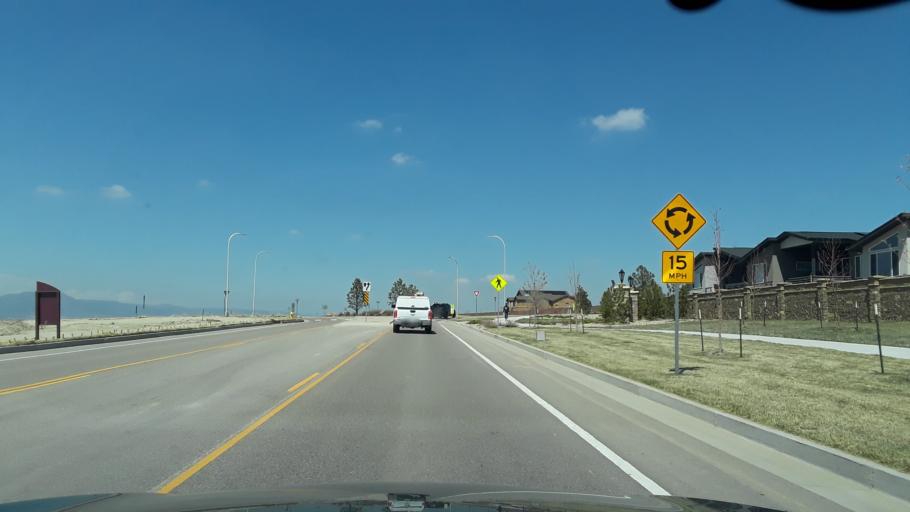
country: US
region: Colorado
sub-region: El Paso County
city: Black Forest
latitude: 38.9827
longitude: -104.7572
